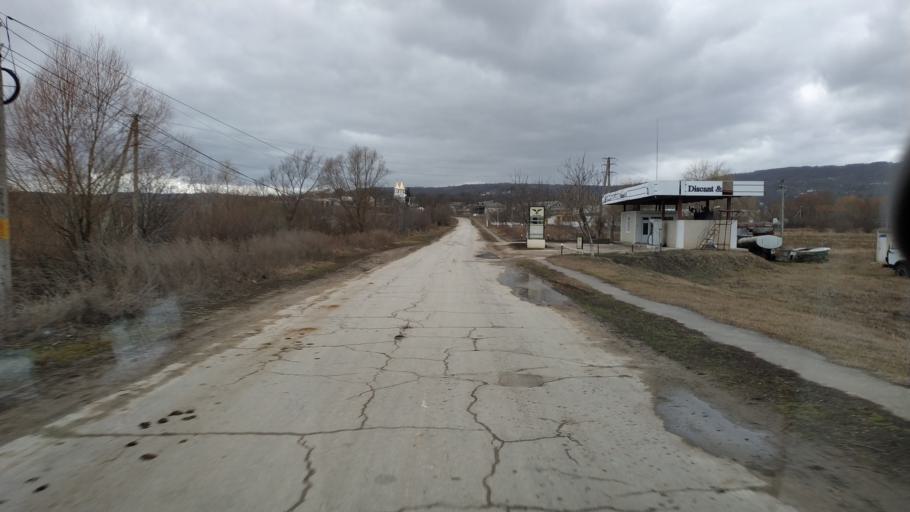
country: MD
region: Calarasi
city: Calarasi
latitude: 47.2548
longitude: 28.1439
